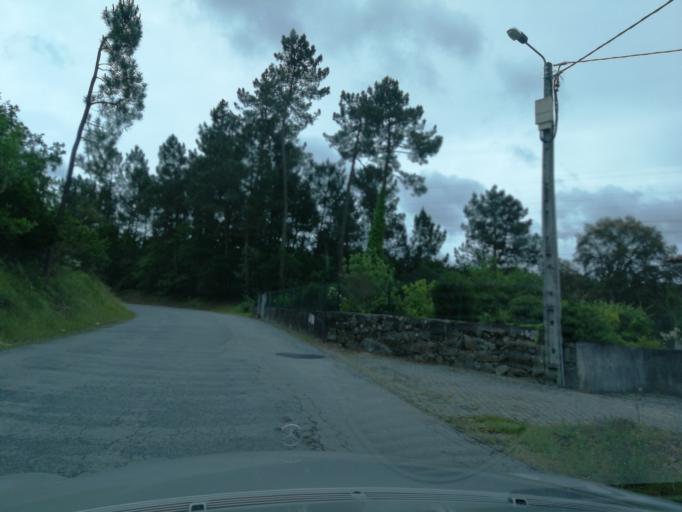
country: PT
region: Braga
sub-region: Braga
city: Adaufe
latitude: 41.6030
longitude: -8.3994
